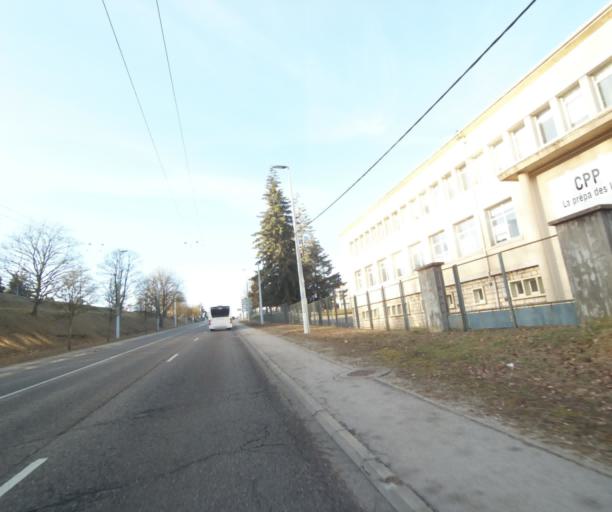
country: FR
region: Lorraine
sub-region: Departement de Meurthe-et-Moselle
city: Villers-les-Nancy
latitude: 48.6558
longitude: 6.1540
